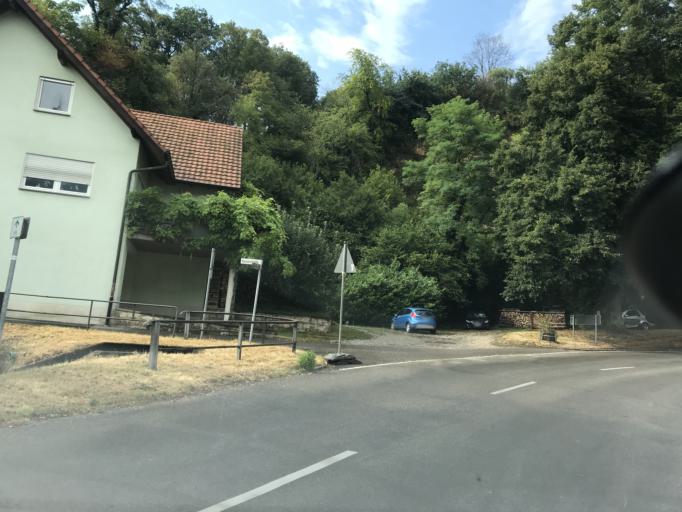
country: DE
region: Baden-Wuerttemberg
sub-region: Freiburg Region
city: Kandern
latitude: 47.7159
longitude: 7.6371
